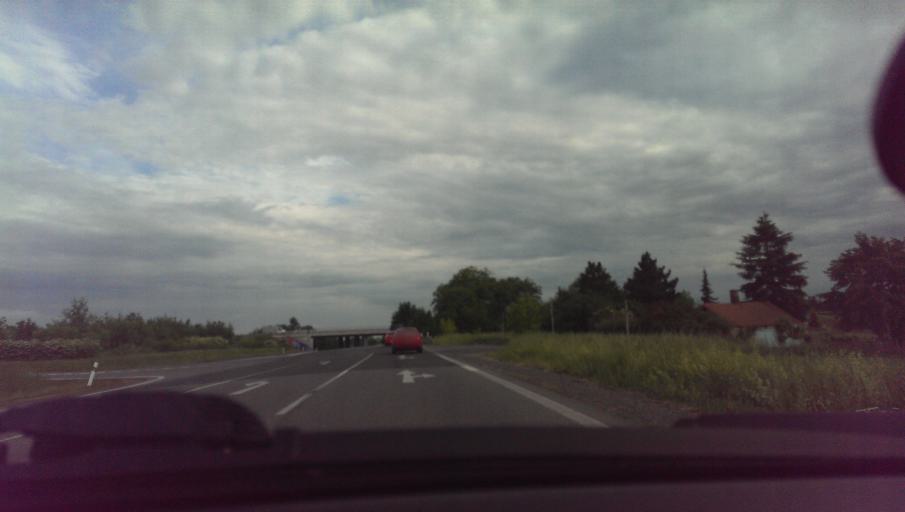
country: CZ
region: Zlin
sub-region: Okres Kromeriz
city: Kromeriz
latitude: 49.3096
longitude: 17.3782
